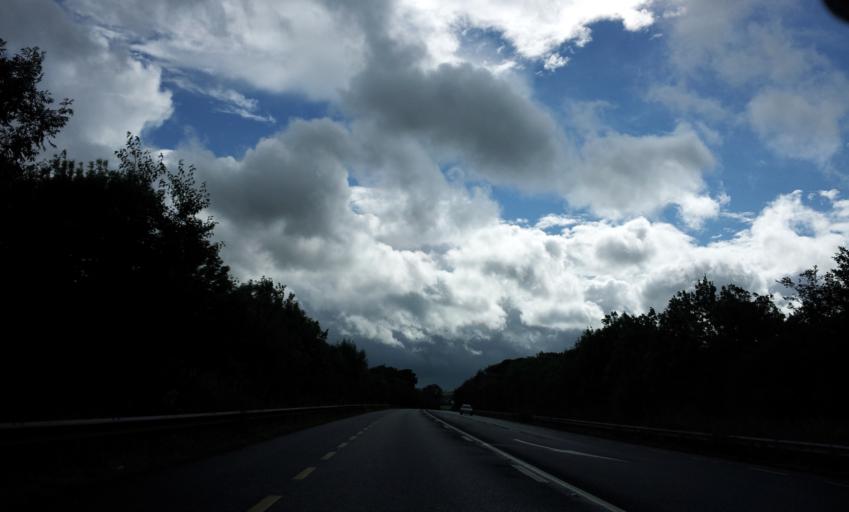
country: IE
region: Munster
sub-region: Waterford
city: Portlaw
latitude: 52.2083
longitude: -7.3984
